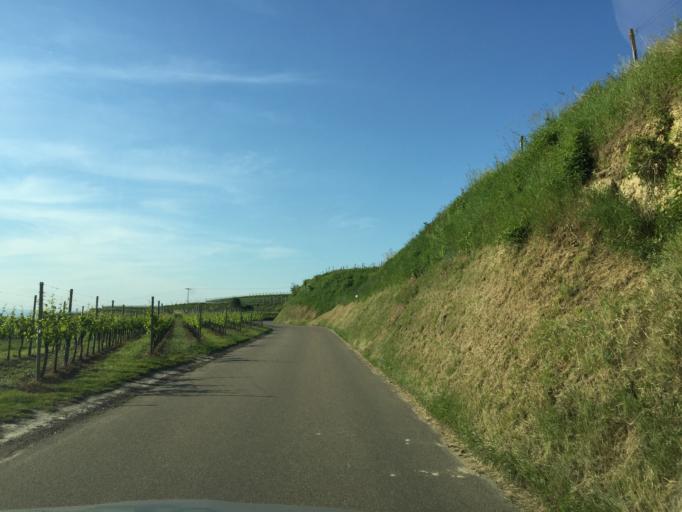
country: DE
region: Baden-Wuerttemberg
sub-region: Freiburg Region
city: Vogtsburg
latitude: 48.0762
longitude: 7.6396
